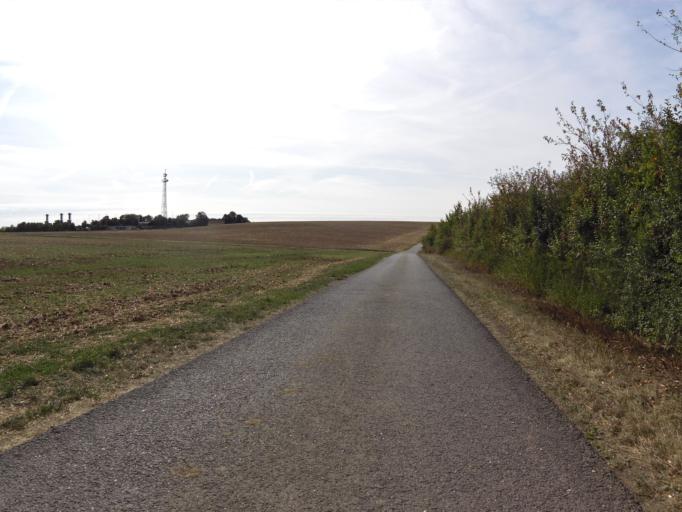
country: DE
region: Bavaria
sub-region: Regierungsbezirk Unterfranken
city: Rimpar
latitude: 49.8440
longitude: 9.9396
